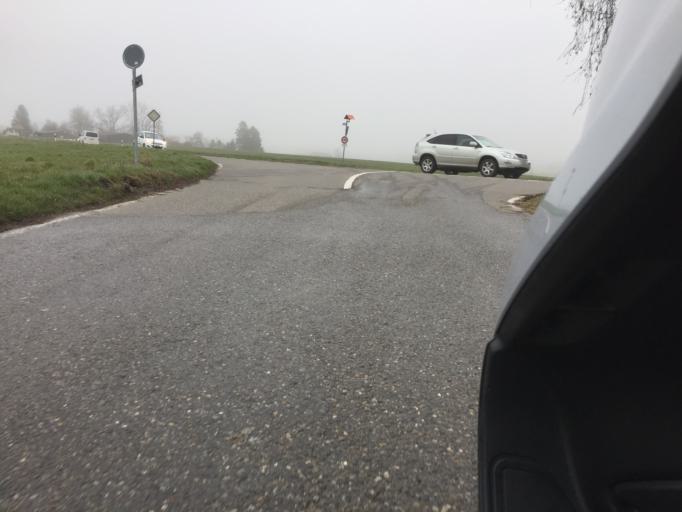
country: CH
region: Bern
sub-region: Seeland District
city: Grossaffoltern
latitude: 47.0814
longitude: 7.3918
